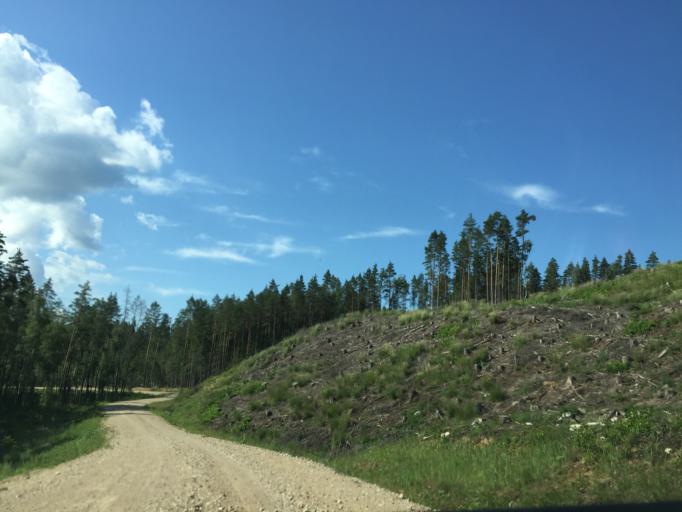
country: LV
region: Tukuma Rajons
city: Tukums
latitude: 57.0129
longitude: 23.2312
